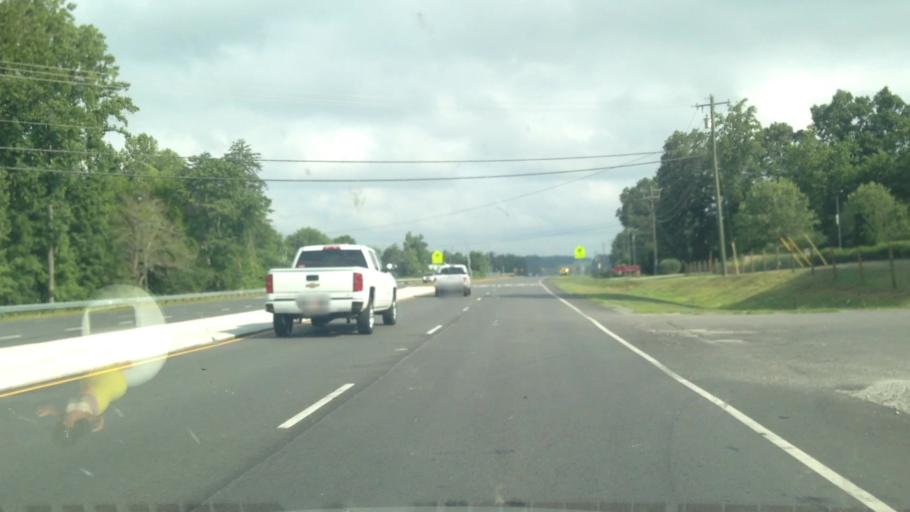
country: US
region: North Carolina
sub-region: Guilford County
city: Summerfield
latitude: 36.2156
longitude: -79.9077
